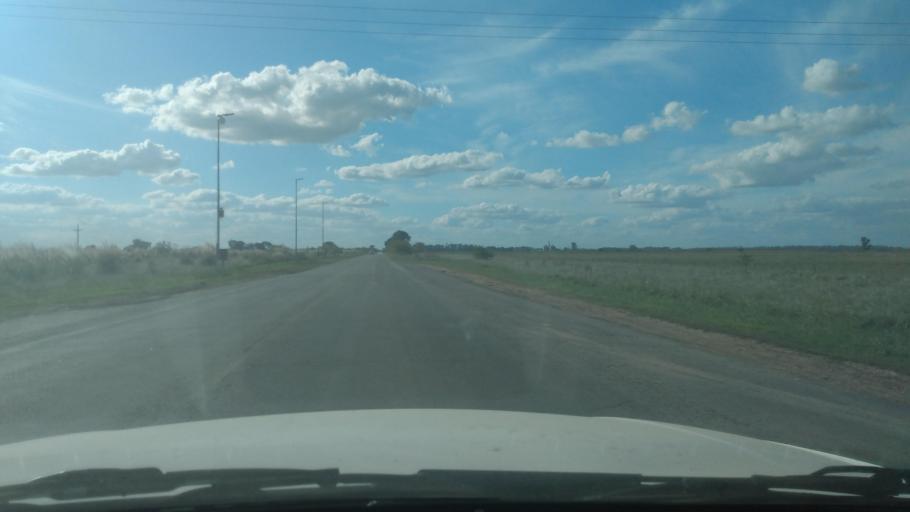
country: AR
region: Buenos Aires
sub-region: Partido de Navarro
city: Navarro
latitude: -34.9858
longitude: -59.3151
